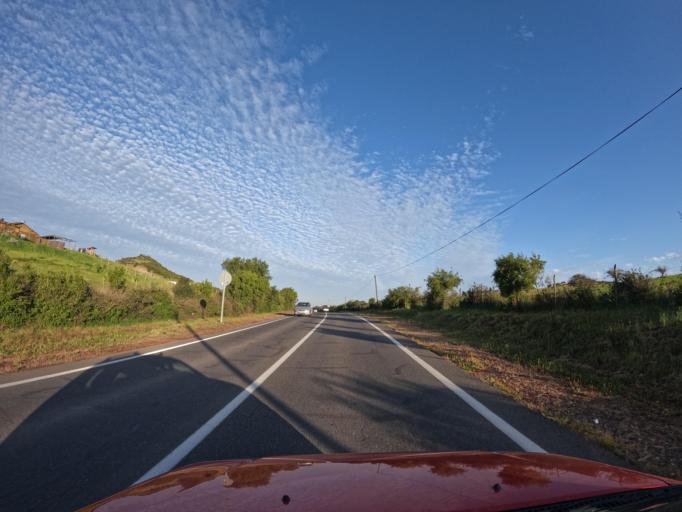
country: CL
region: O'Higgins
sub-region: Provincia de Colchagua
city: Santa Cruz
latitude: -34.2088
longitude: -71.7320
